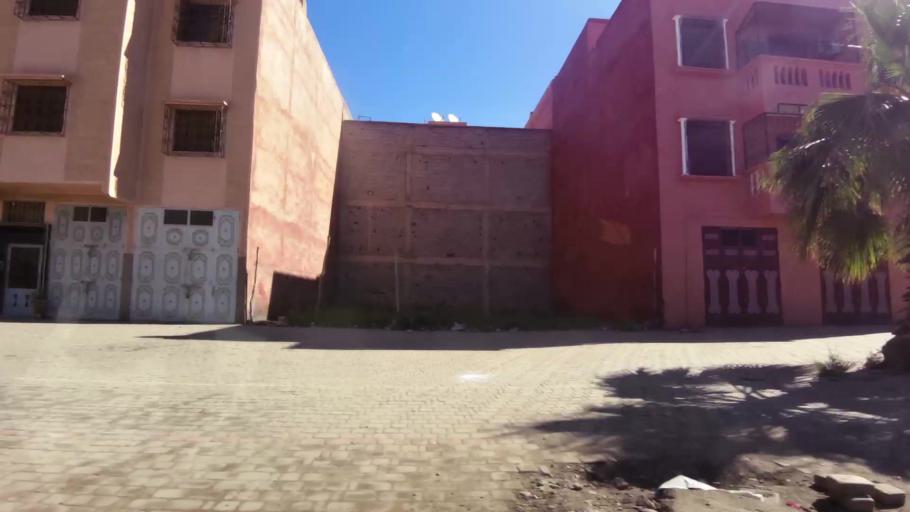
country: MA
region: Marrakech-Tensift-Al Haouz
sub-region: Marrakech
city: Marrakesh
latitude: 31.5960
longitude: -8.0486
